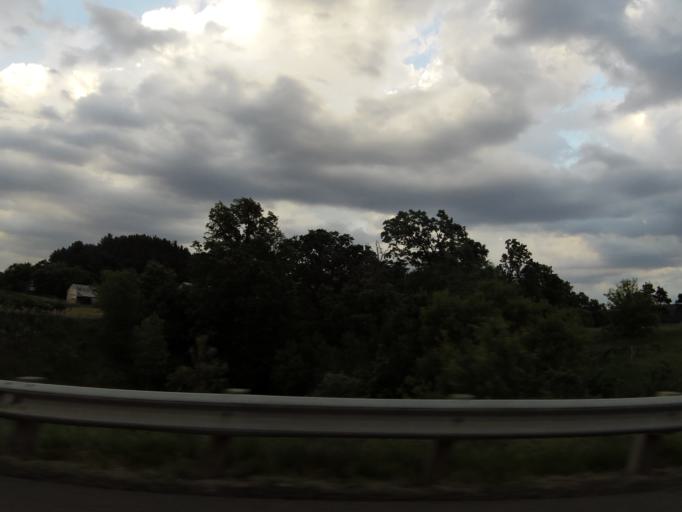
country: US
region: Wisconsin
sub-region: Eau Claire County
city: Altoona
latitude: 44.7381
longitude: -91.3728
